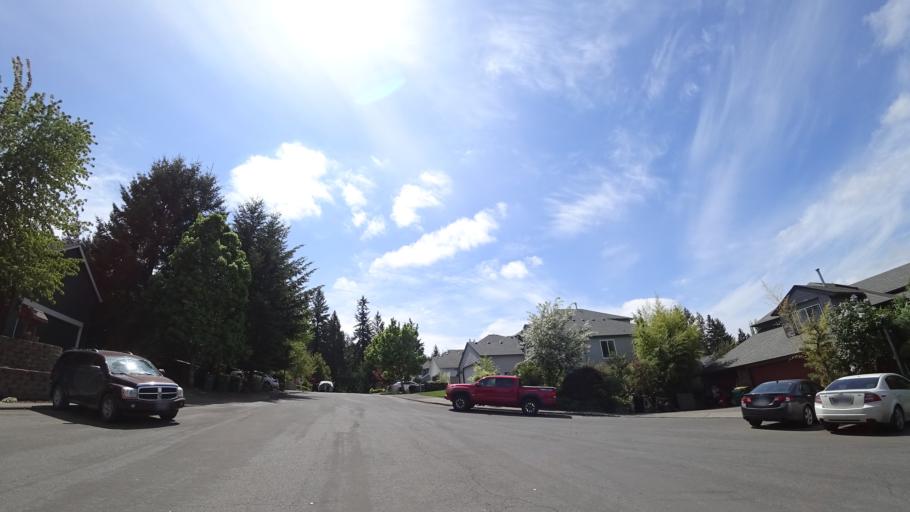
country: US
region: Oregon
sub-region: Washington County
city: Aloha
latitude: 45.4656
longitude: -122.8886
